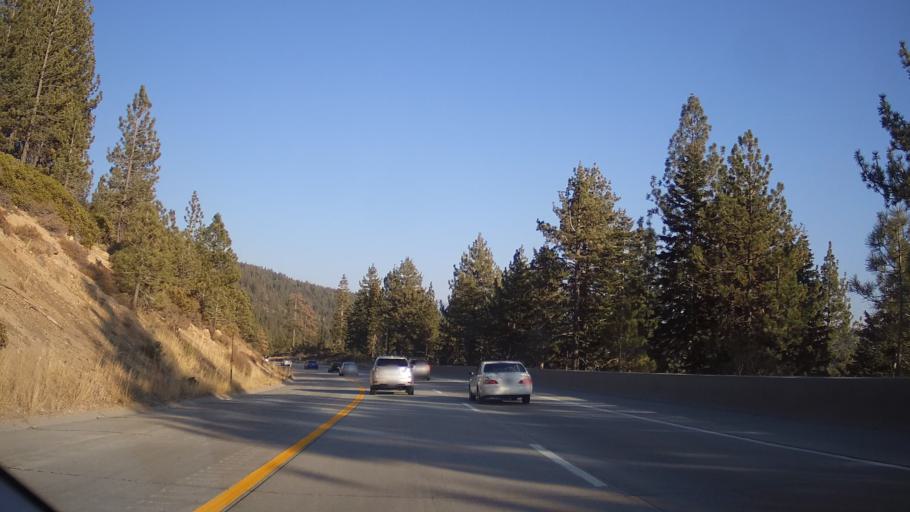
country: US
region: California
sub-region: Nevada County
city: Truckee
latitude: 39.3292
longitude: -120.2651
